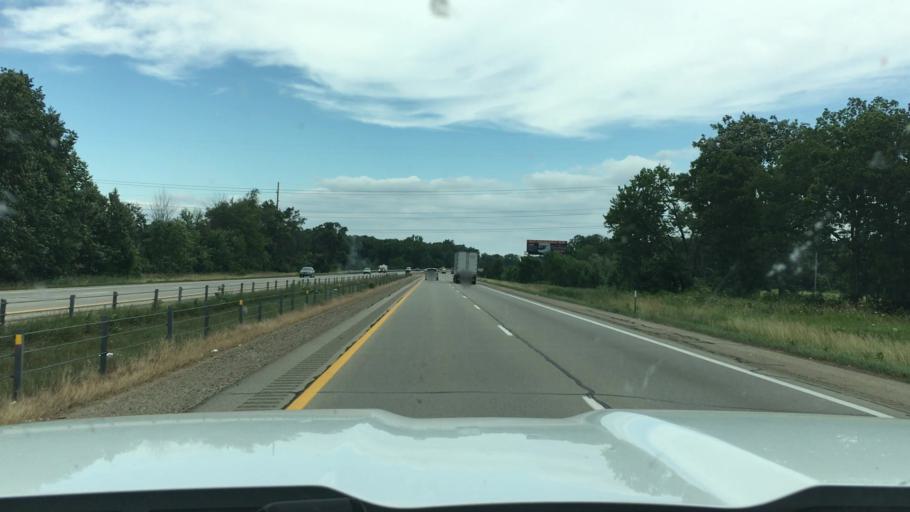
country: US
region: Michigan
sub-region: Kent County
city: Byron Center
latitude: 42.7572
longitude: -85.6735
